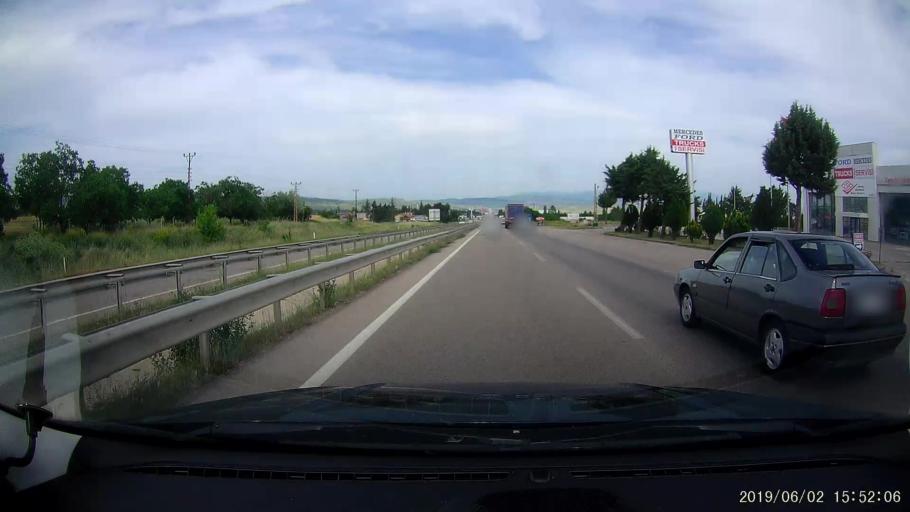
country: TR
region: Amasya
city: Merzifon
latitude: 40.8709
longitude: 35.5070
